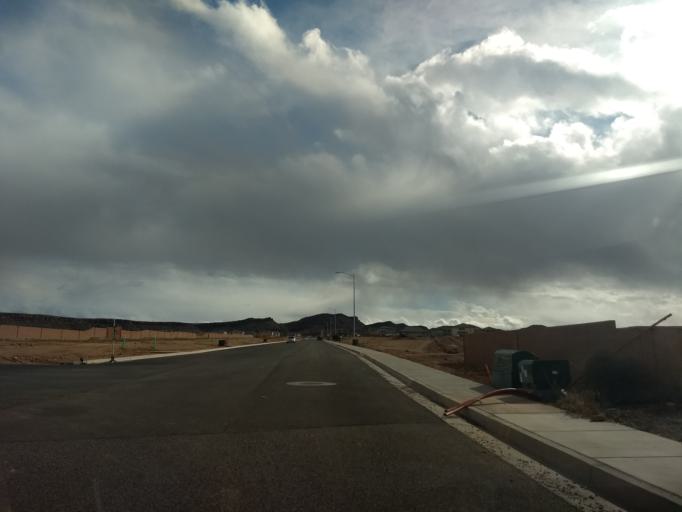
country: US
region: Utah
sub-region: Washington County
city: Washington
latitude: 37.0632
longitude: -113.5177
